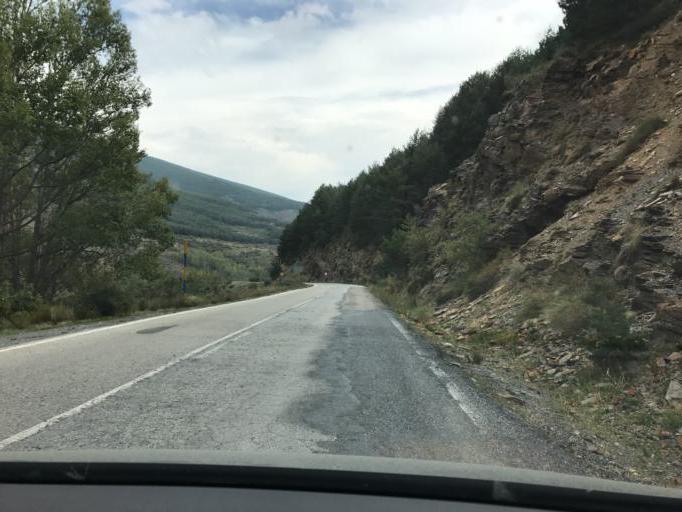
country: ES
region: Andalusia
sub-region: Provincia de Almeria
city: Bayarcal
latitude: 37.0907
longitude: -3.0289
